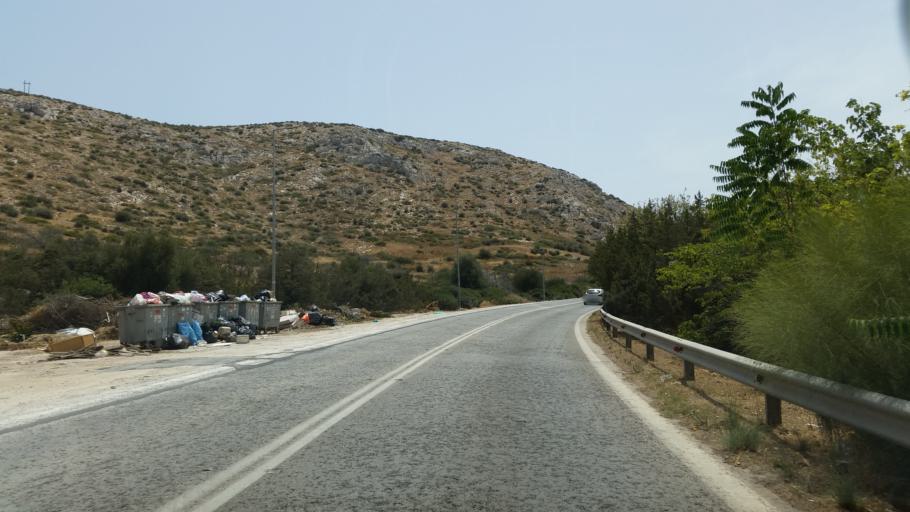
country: GR
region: Attica
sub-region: Nomarchia Anatolikis Attikis
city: Palaia Fokaia
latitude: 37.7120
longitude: 23.9424
